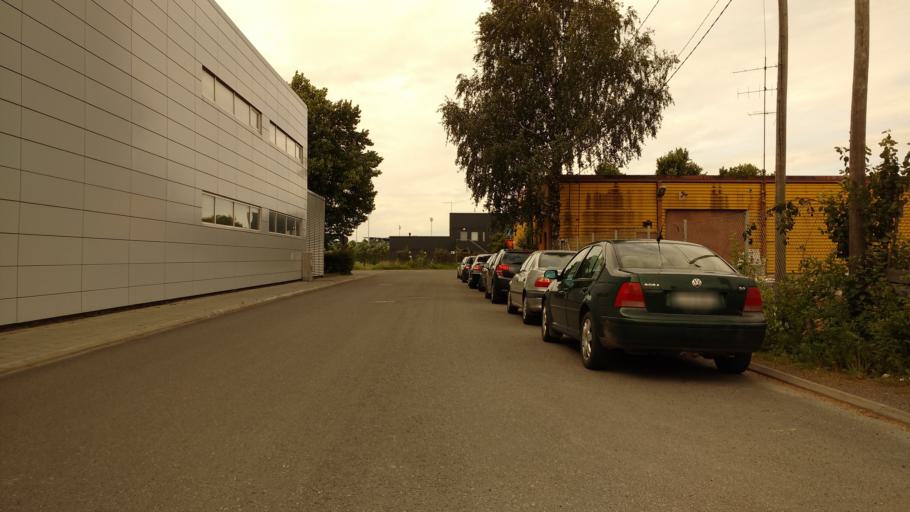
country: FI
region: Varsinais-Suomi
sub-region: Turku
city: Turku
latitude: 60.4476
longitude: 22.2981
